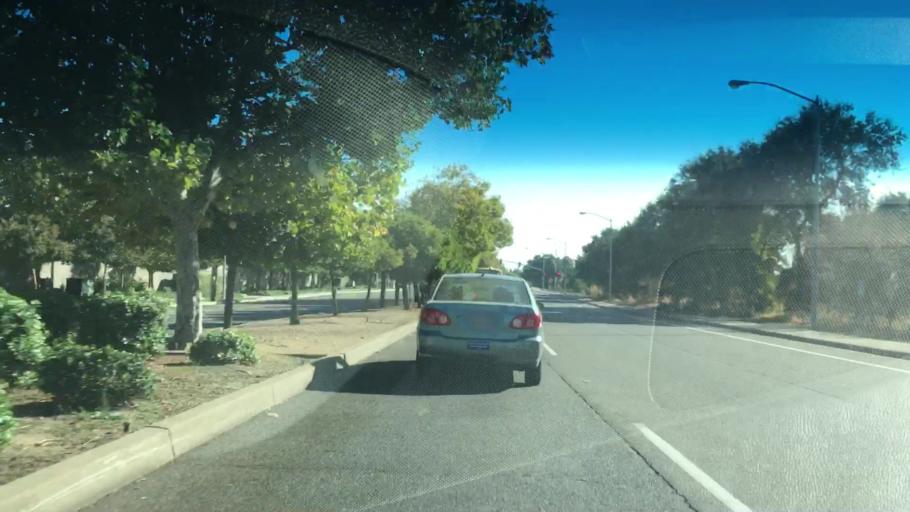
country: US
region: California
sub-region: Sacramento County
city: Laguna
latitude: 38.4506
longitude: -121.4447
